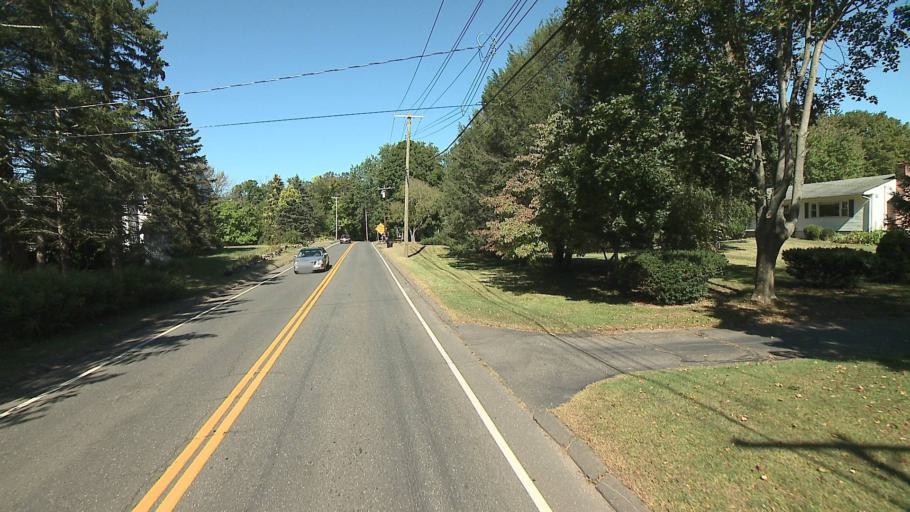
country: US
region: Connecticut
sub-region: New Haven County
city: Orange
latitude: 41.2640
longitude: -73.0509
